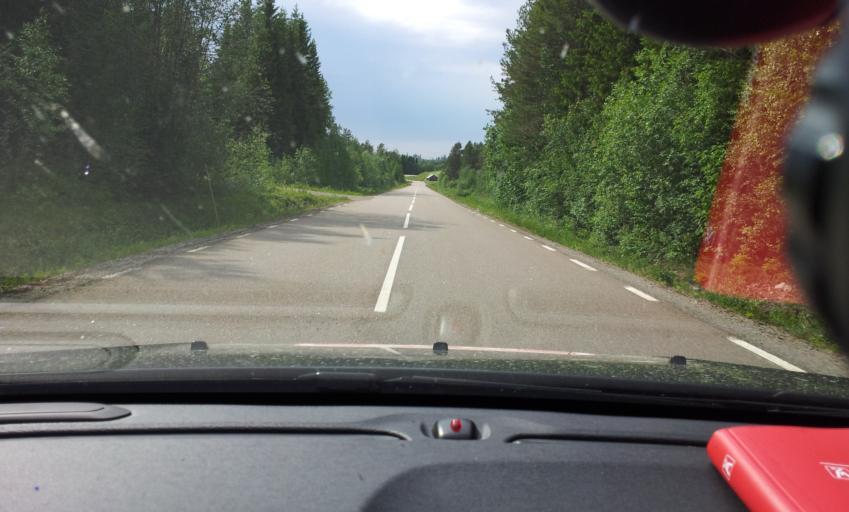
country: SE
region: Jaemtland
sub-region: OEstersunds Kommun
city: Brunflo
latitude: 62.6606
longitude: 14.8711
